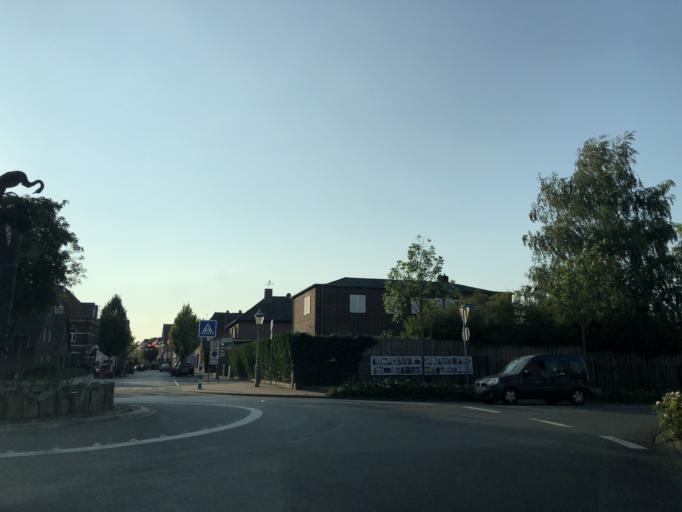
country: DE
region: North Rhine-Westphalia
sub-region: Regierungsbezirk Dusseldorf
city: Kranenburg
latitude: 51.7886
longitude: 6.0114
